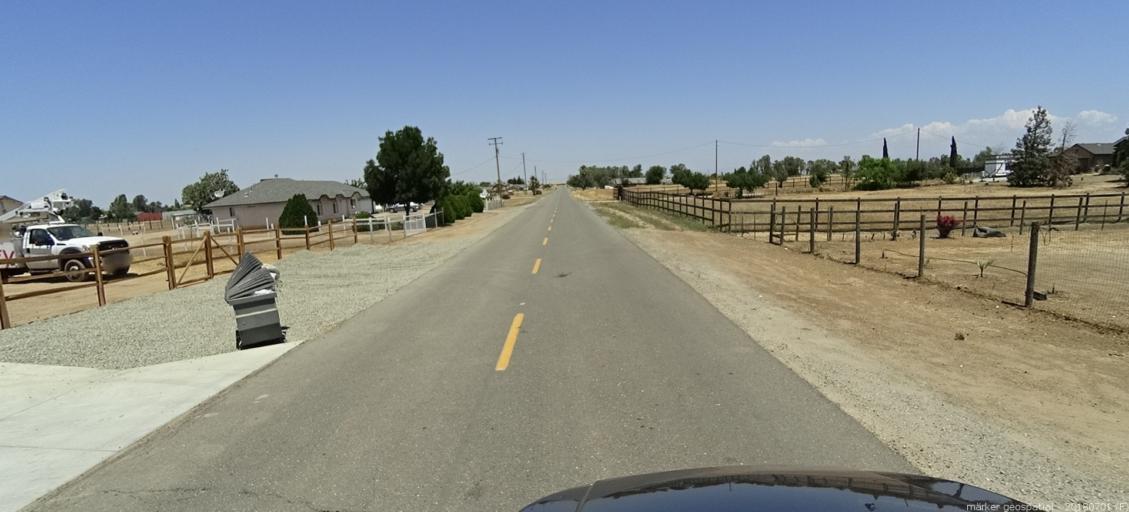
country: US
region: California
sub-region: Madera County
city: Madera Acres
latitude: 37.0441
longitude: -119.9958
